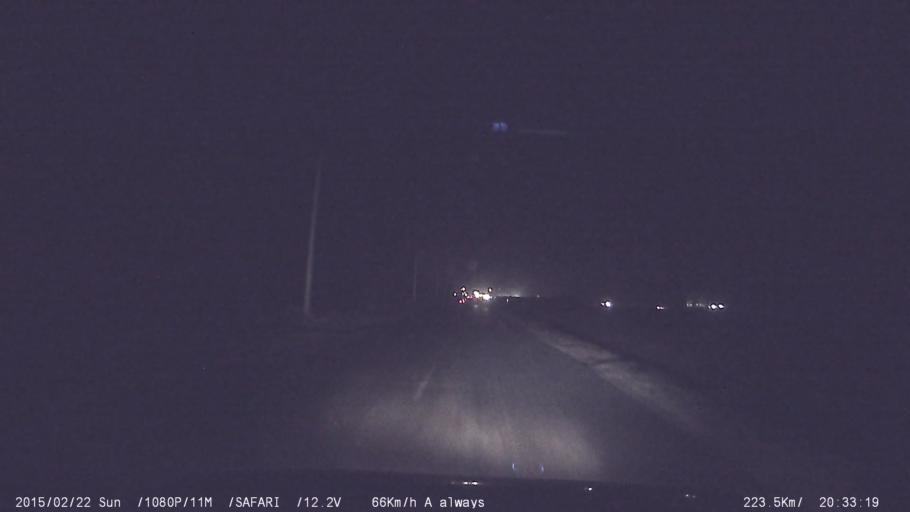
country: IN
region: Tamil Nadu
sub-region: Dindigul
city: Dindigul
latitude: 10.3562
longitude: 77.9495
